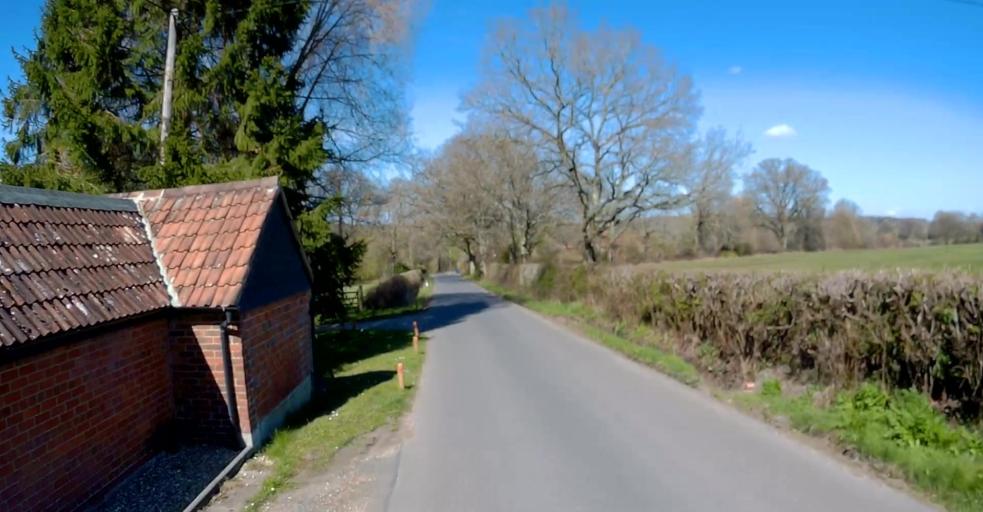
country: GB
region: England
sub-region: Hampshire
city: Lindford
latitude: 51.1658
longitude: -0.8285
